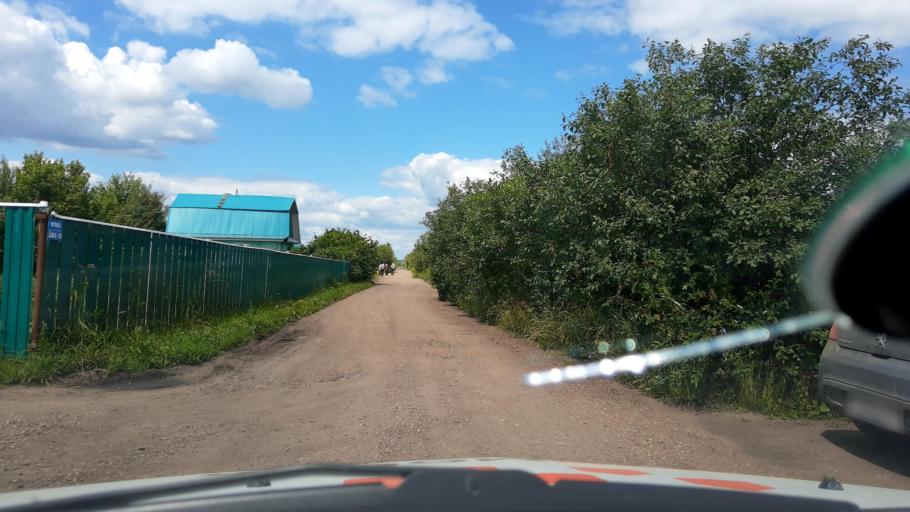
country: RU
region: Bashkortostan
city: Kabakovo
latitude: 54.7219
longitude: 56.2071
